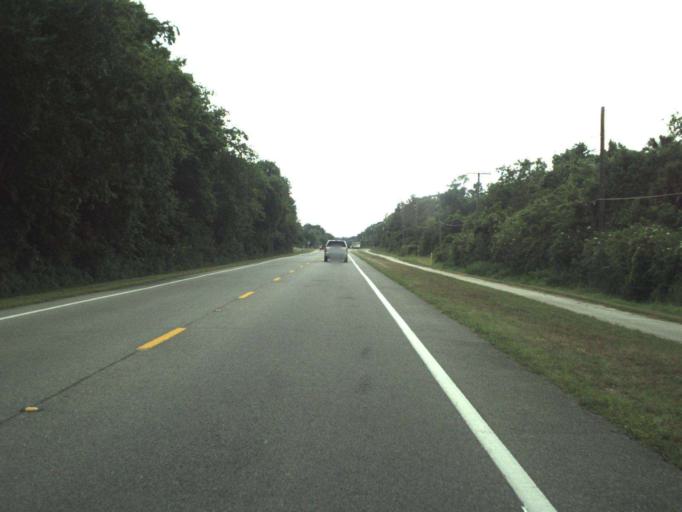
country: US
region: Florida
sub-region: Brevard County
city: Titusville
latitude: 28.6040
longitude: -80.8343
